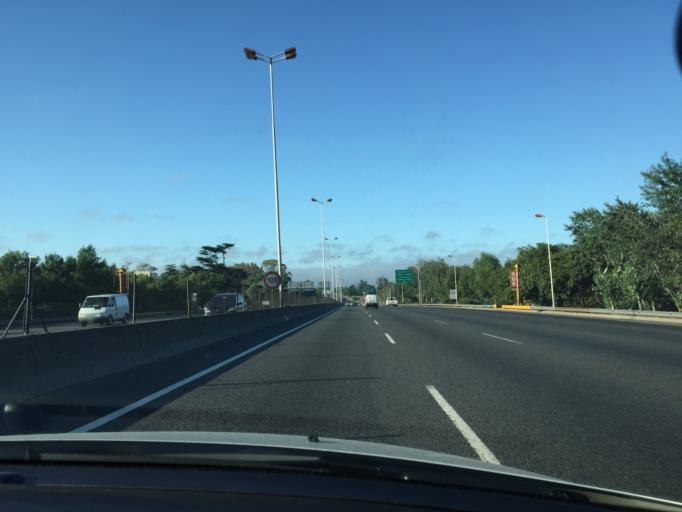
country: AR
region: Buenos Aires F.D.
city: Villa Lugano
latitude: -34.7153
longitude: -58.5088
